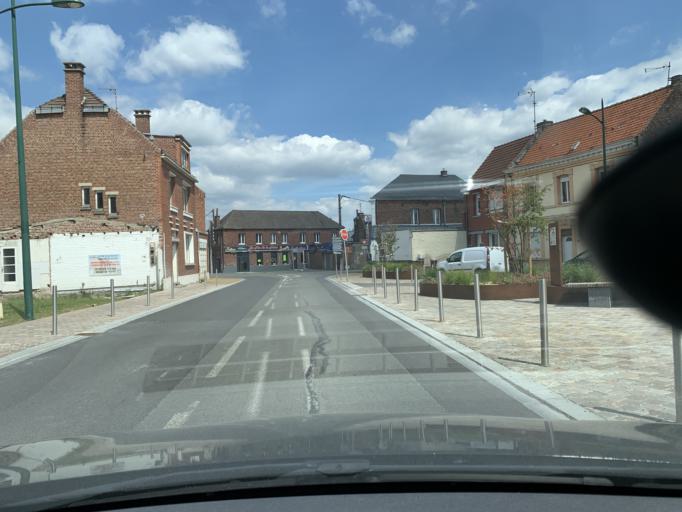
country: FR
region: Nord-Pas-de-Calais
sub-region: Departement du Nord
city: Arleux
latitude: 50.2811
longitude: 3.1052
